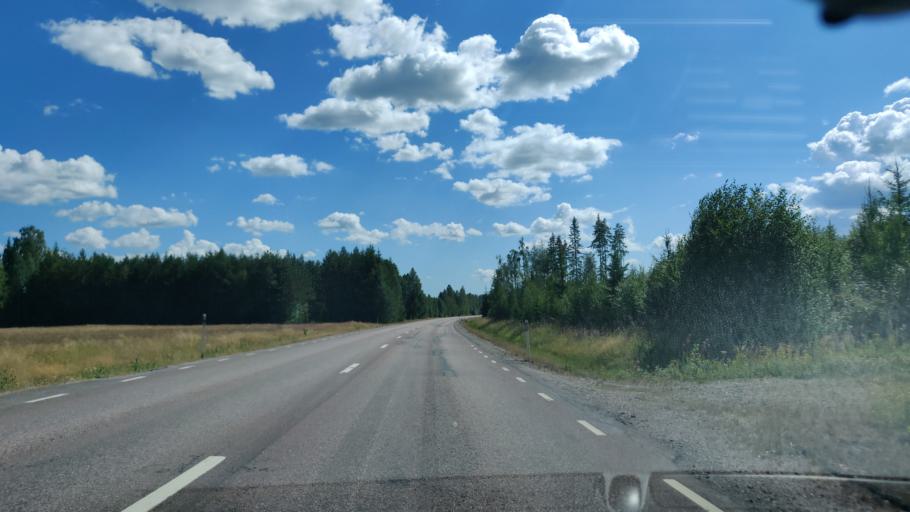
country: SE
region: Vaermland
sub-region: Hagfors Kommun
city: Ekshaerad
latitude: 60.2062
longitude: 13.4901
